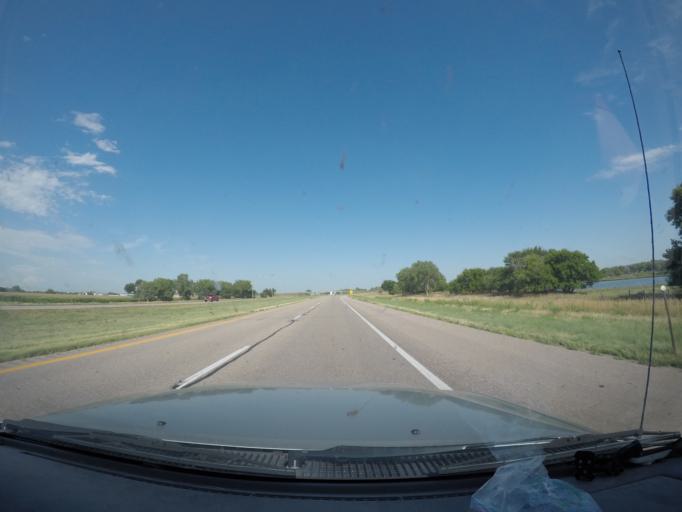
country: US
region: Nebraska
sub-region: Phelps County
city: Holdrege
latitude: 40.6901
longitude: -99.3874
